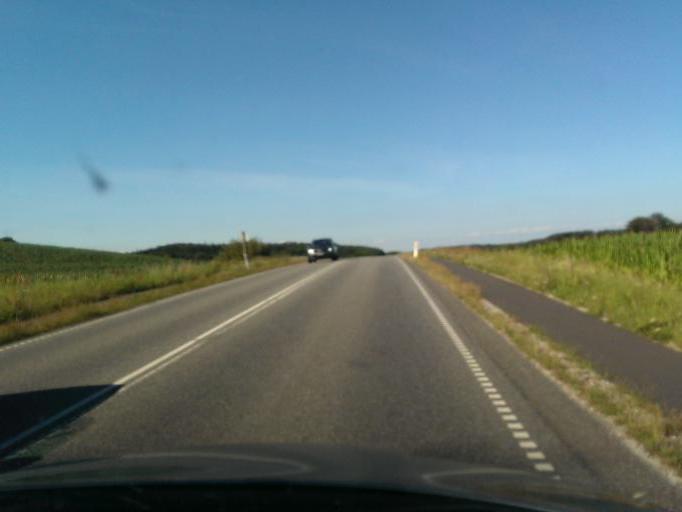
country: DK
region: Central Jutland
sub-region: Odder Kommune
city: Odder
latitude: 55.9413
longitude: 10.1500
